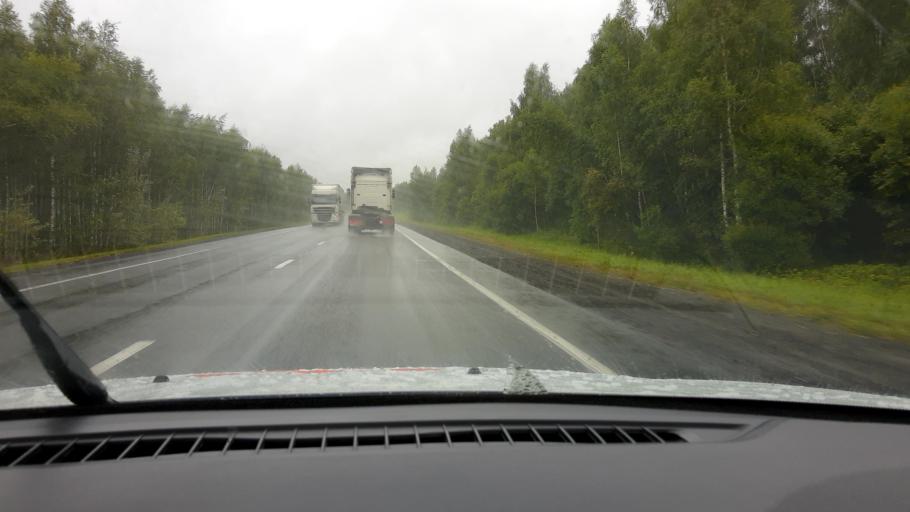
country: RU
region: Nizjnij Novgorod
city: Spasskoye
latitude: 56.0491
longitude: 45.5625
